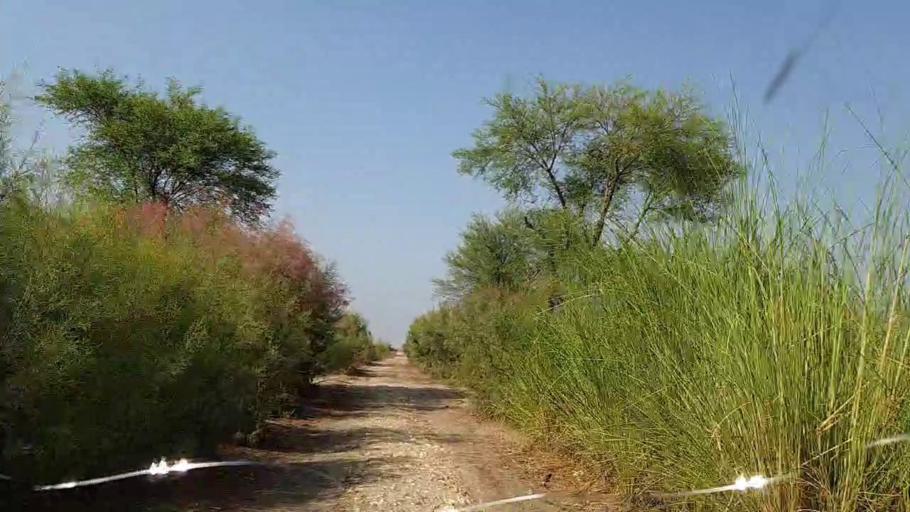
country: PK
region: Sindh
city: Khanpur
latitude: 27.6821
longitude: 69.3785
